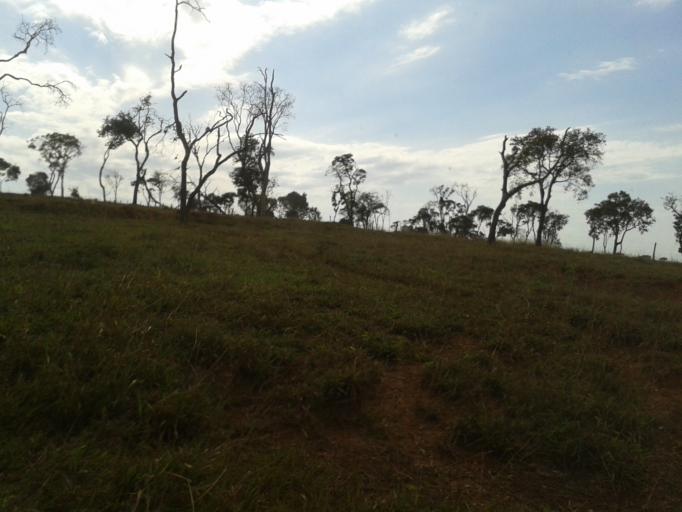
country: BR
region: Minas Gerais
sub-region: Ituiutaba
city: Ituiutaba
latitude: -19.0754
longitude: -49.3614
